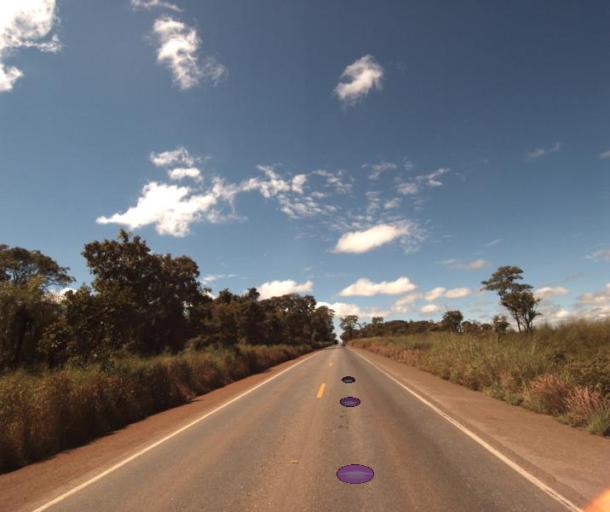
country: BR
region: Goias
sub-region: Rialma
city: Rialma
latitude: -15.4038
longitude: -49.5335
